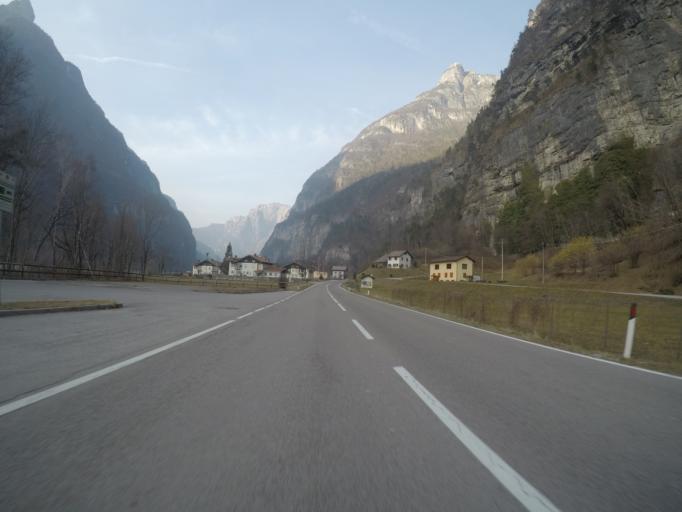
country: IT
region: Veneto
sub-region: Provincia di Belluno
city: Sospirolo
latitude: 46.2135
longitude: 12.1287
